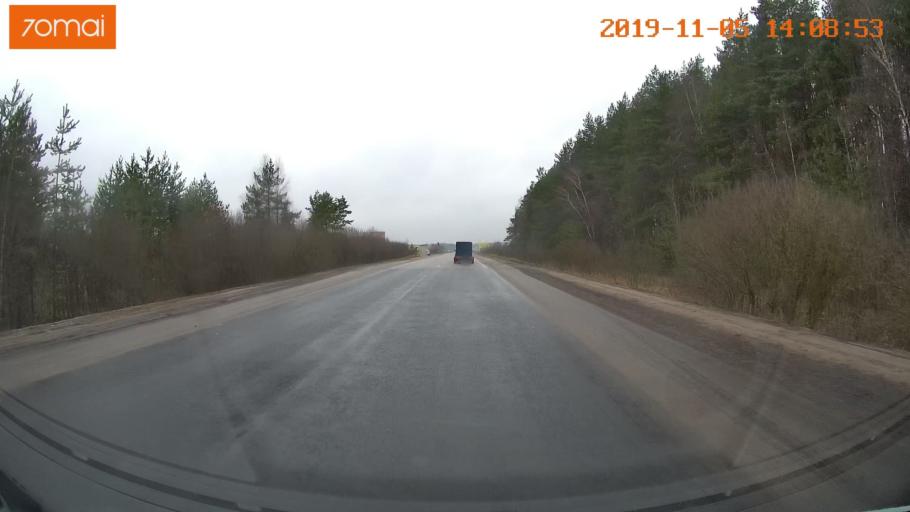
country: RU
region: Ivanovo
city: Kokhma
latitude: 56.9835
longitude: 41.0982
